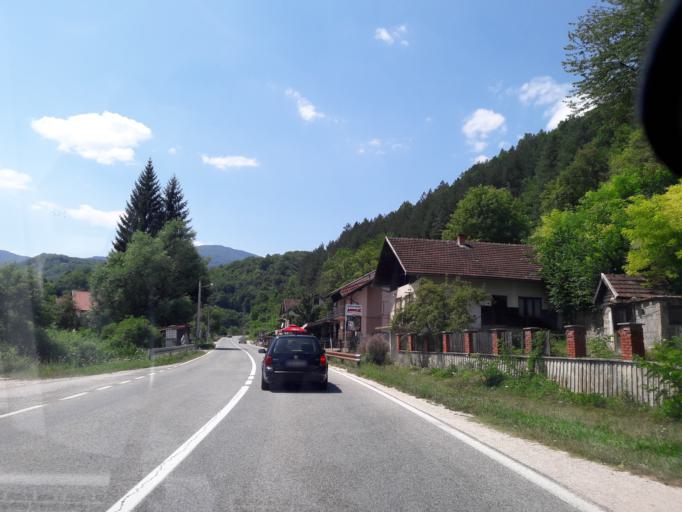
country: BA
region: Republika Srpska
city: Mrkonjic Grad
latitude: 44.3767
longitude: 17.1339
